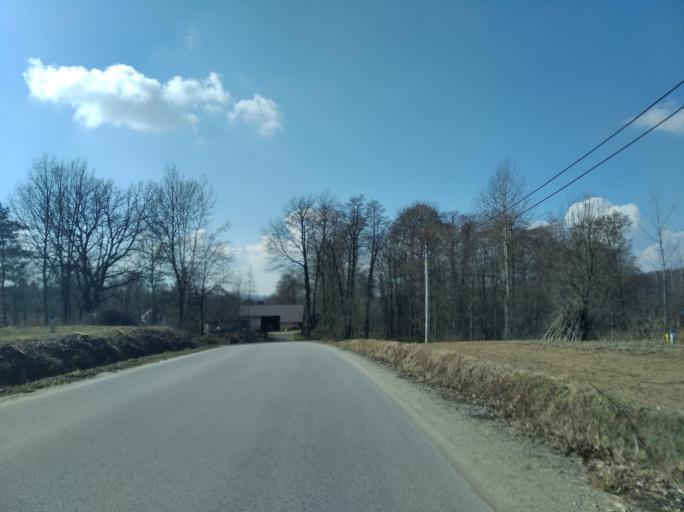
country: PL
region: Subcarpathian Voivodeship
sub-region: Powiat debicki
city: Brzostek
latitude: 49.8874
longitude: 21.4655
